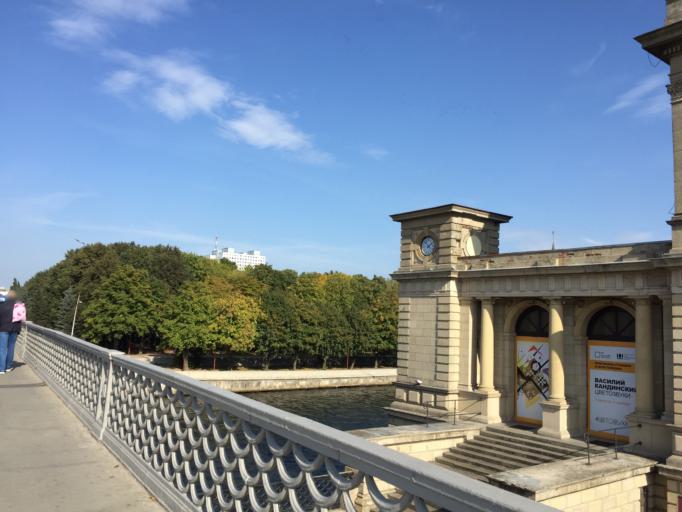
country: RU
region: Kaliningrad
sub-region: Gorod Kaliningrad
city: Kaliningrad
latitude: 54.7052
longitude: 20.5065
